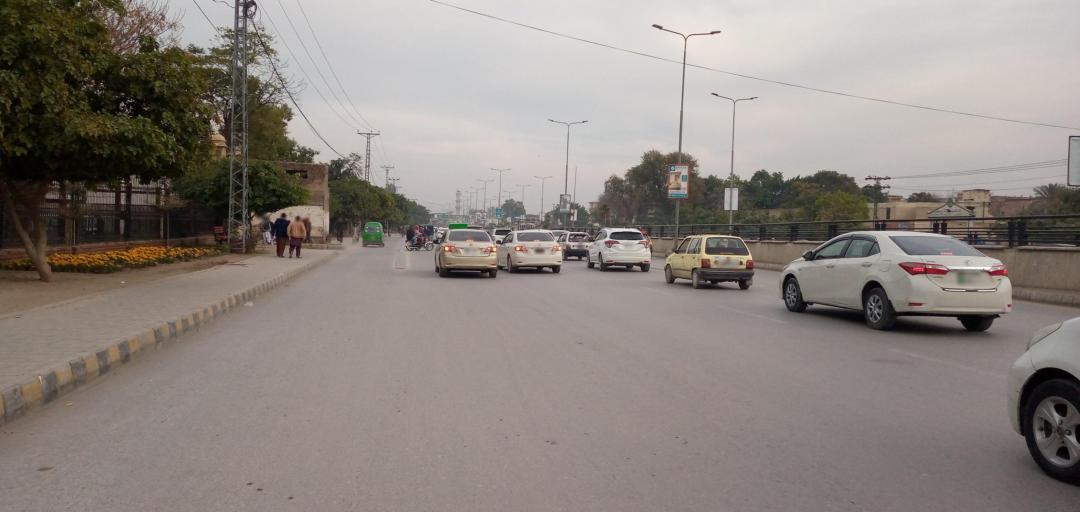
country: PK
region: Khyber Pakhtunkhwa
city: Peshawar
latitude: 33.9983
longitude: 71.4812
